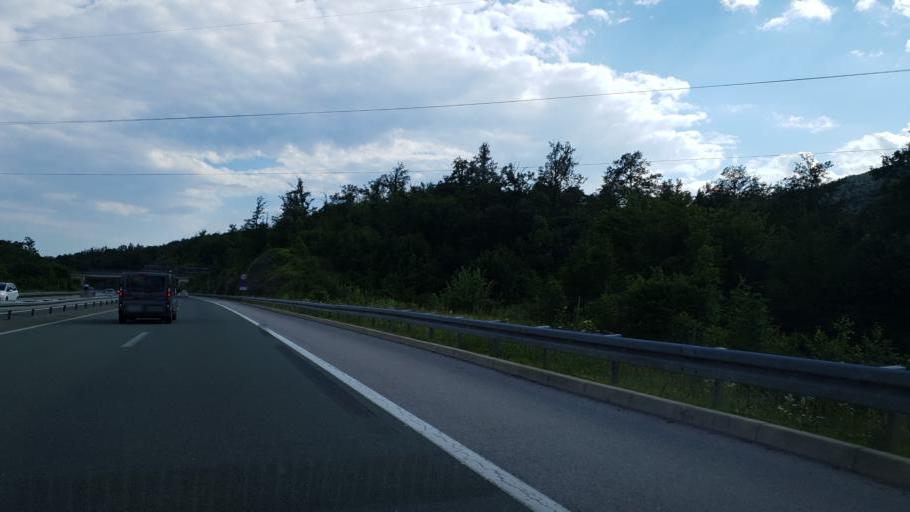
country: HR
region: Primorsko-Goranska
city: Matulji
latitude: 45.3924
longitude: 14.3005
